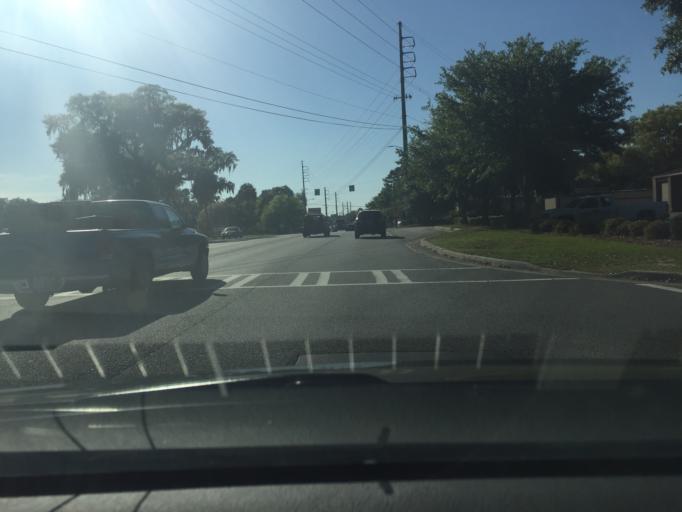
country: US
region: Georgia
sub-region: Chatham County
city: Isle of Hope
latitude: 31.9965
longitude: -81.1152
